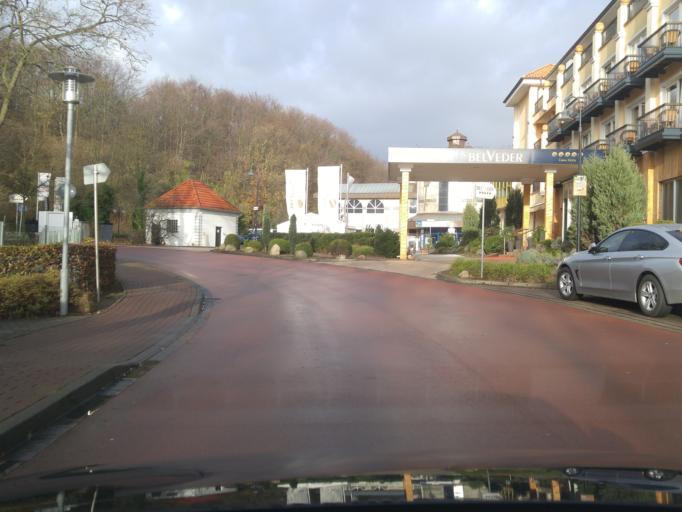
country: DE
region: Schleswig-Holstein
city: Timmendorfer Strand
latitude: 54.0096
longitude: 10.7701
